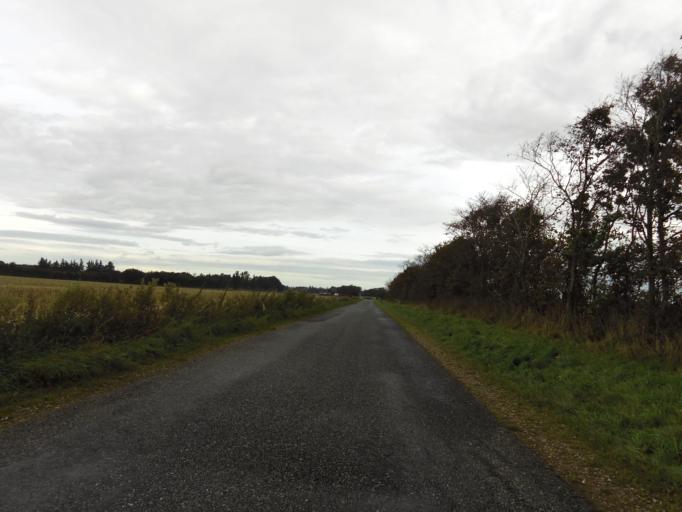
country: DK
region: South Denmark
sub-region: Esbjerg Kommune
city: Ribe
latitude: 55.2719
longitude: 8.8231
